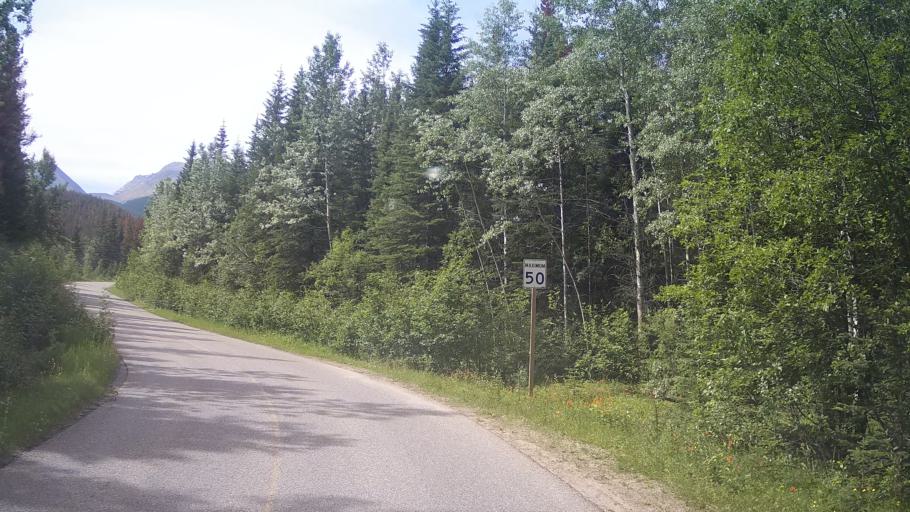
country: CA
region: Alberta
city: Hinton
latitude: 53.1786
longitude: -117.8396
